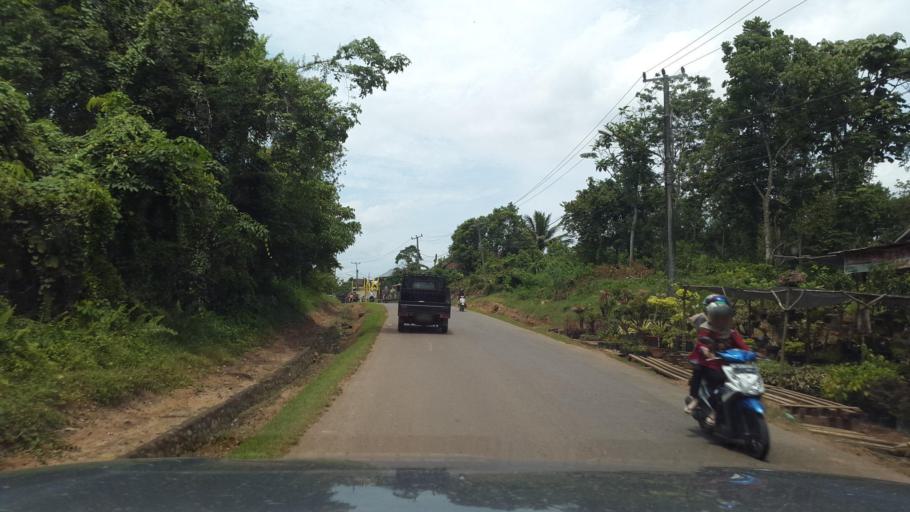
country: ID
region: South Sumatra
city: Gunungmegang Dalam
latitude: -3.2846
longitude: 103.8351
